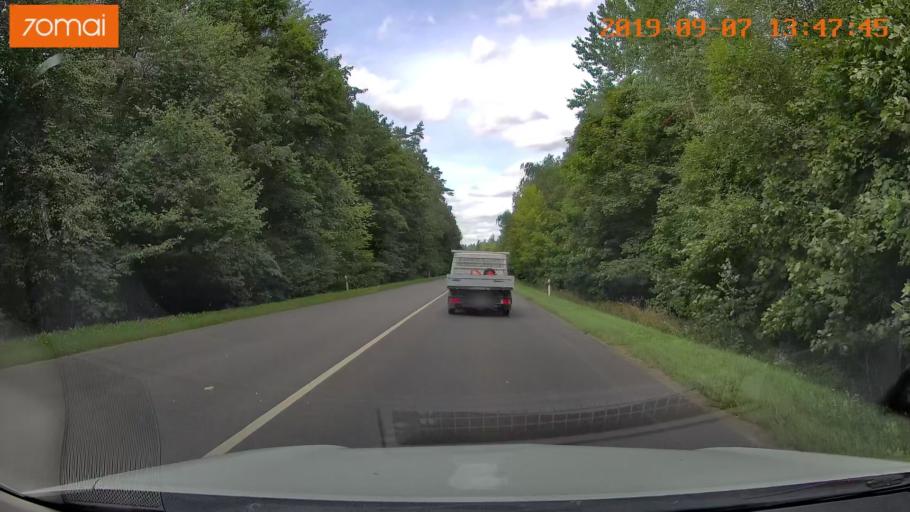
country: LT
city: Baltoji Voke
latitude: 54.5991
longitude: 25.2101
